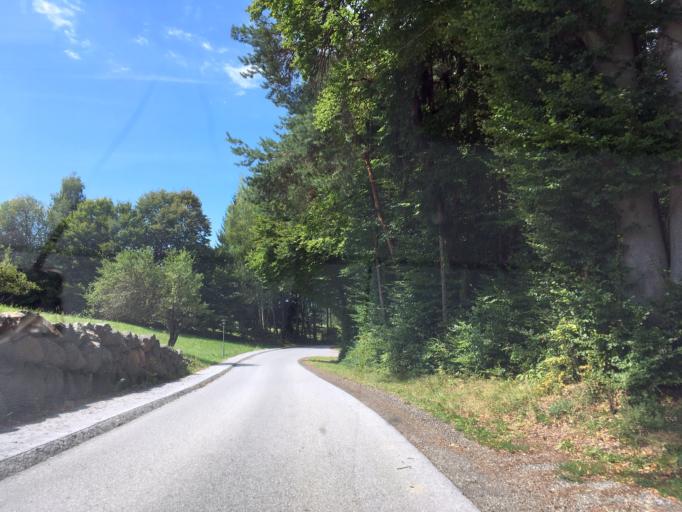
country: AT
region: Styria
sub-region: Politischer Bezirk Leibnitz
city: Pistorf
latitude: 46.7929
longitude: 15.3878
